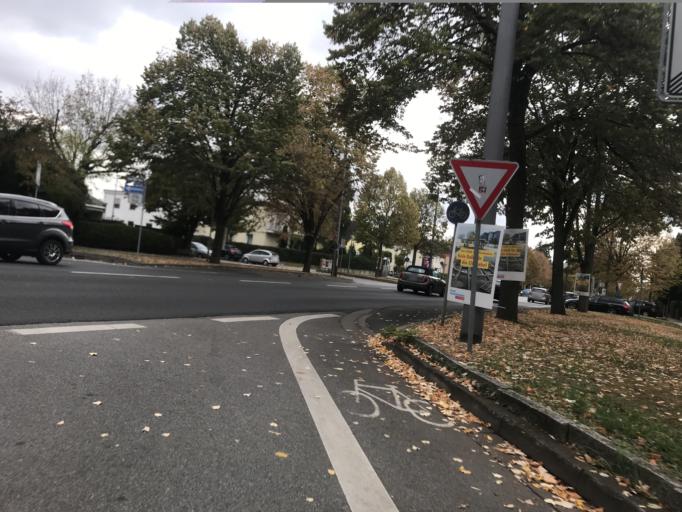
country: DE
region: Hesse
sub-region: Regierungsbezirk Darmstadt
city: Wiesbaden
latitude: 50.0571
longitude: 8.2431
